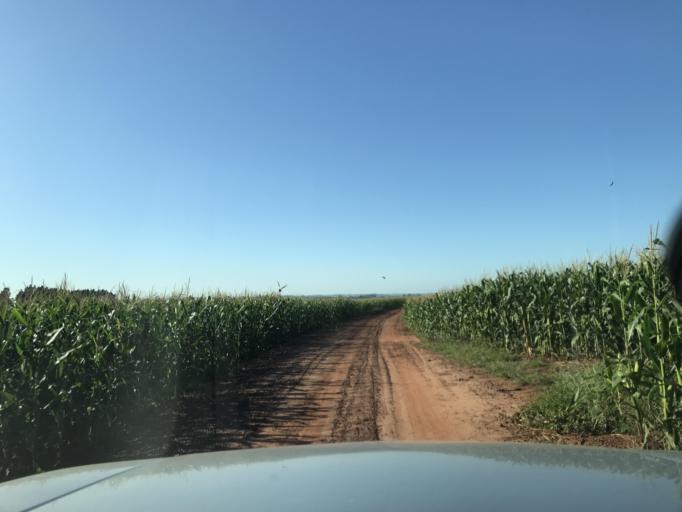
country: BR
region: Parana
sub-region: Palotina
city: Palotina
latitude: -24.2350
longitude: -53.7729
